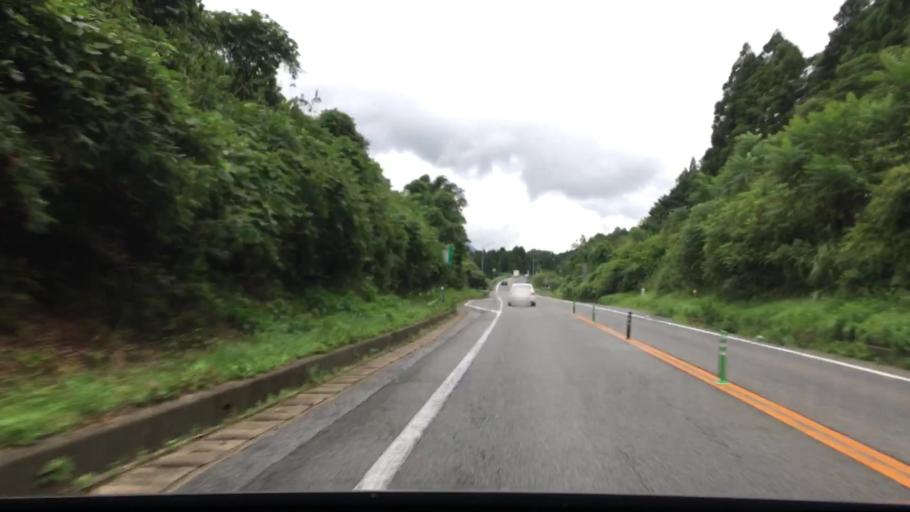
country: JP
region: Hyogo
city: Nishiwaki
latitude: 35.1015
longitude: 134.7774
